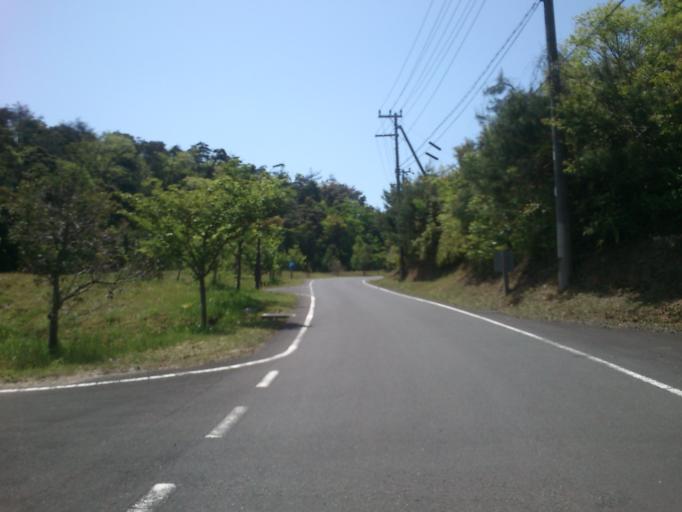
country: JP
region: Kyoto
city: Miyazu
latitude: 35.6222
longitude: 135.2378
